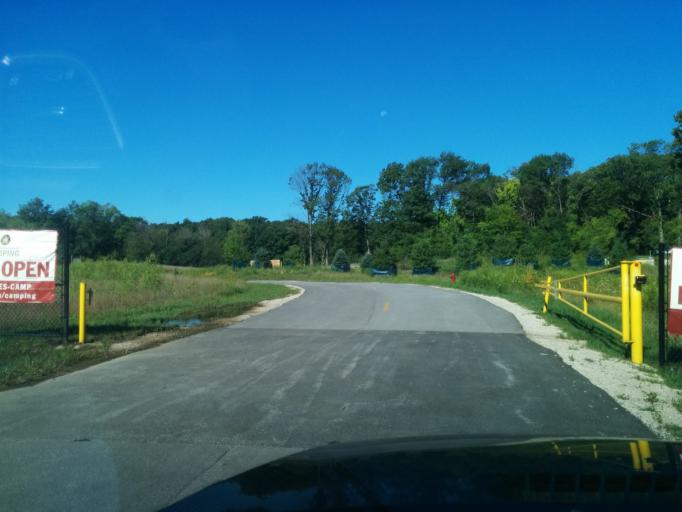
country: US
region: Illinois
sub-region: Cook County
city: Palos Heights
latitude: 41.6263
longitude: -87.7850
